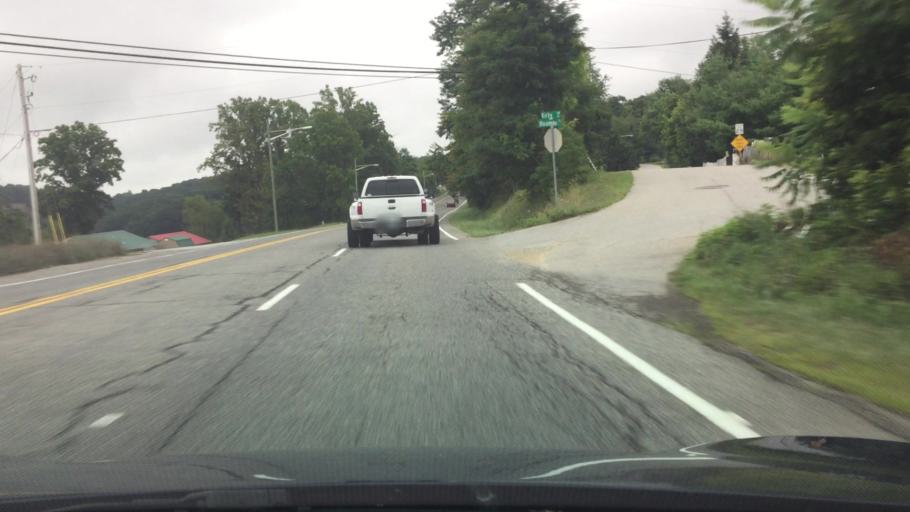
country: US
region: Virginia
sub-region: Montgomery County
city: Christiansburg
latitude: 37.1392
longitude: -80.3364
